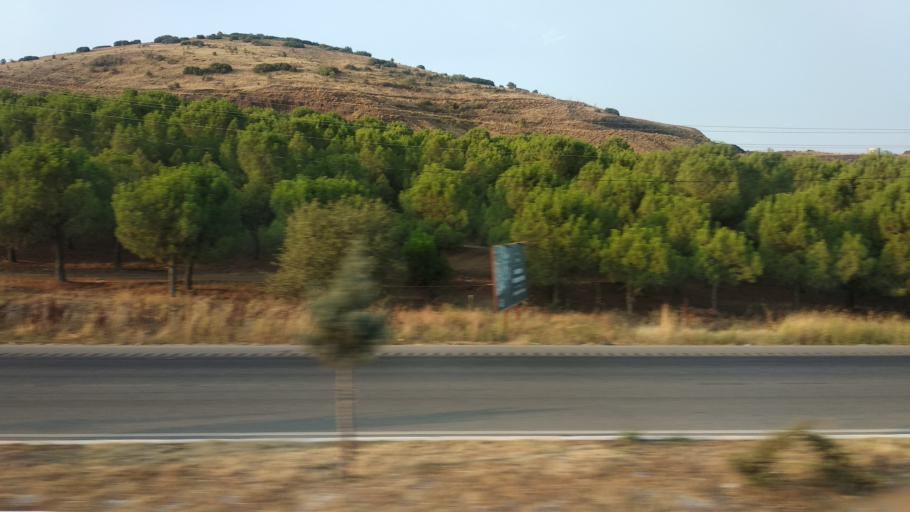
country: TR
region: Manisa
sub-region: Kula
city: Kula
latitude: 38.5677
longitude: 28.5788
